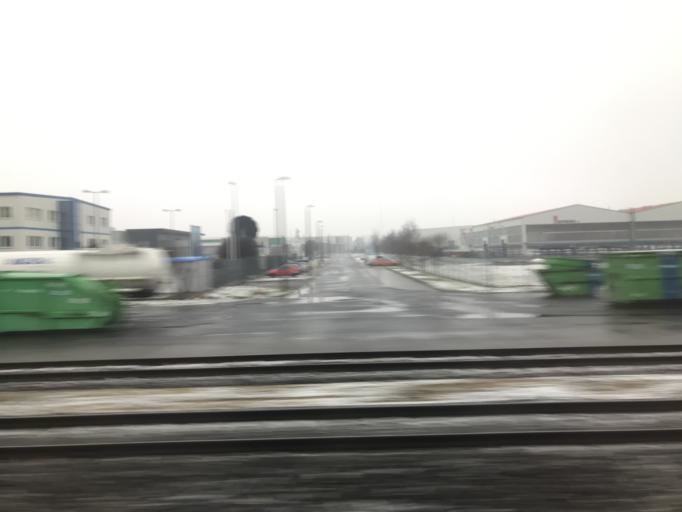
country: HU
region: Gyor-Moson-Sopron
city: Gyor
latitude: 47.6837
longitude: 17.6941
